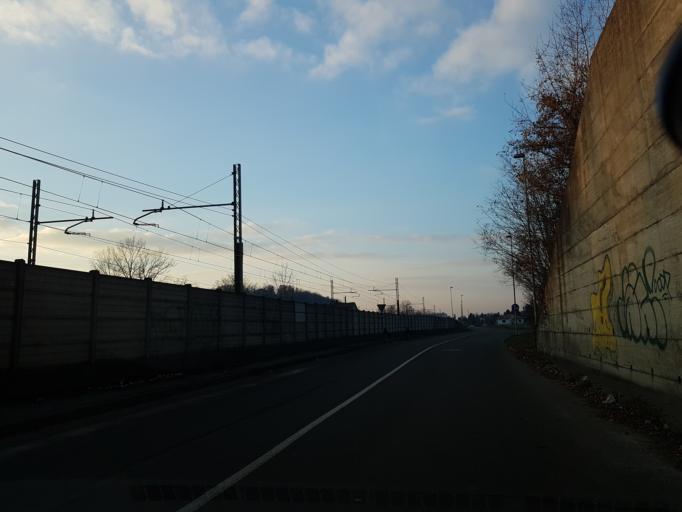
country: IT
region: Piedmont
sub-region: Provincia di Alessandria
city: Novi Ligure
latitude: 44.7528
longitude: 8.8072
